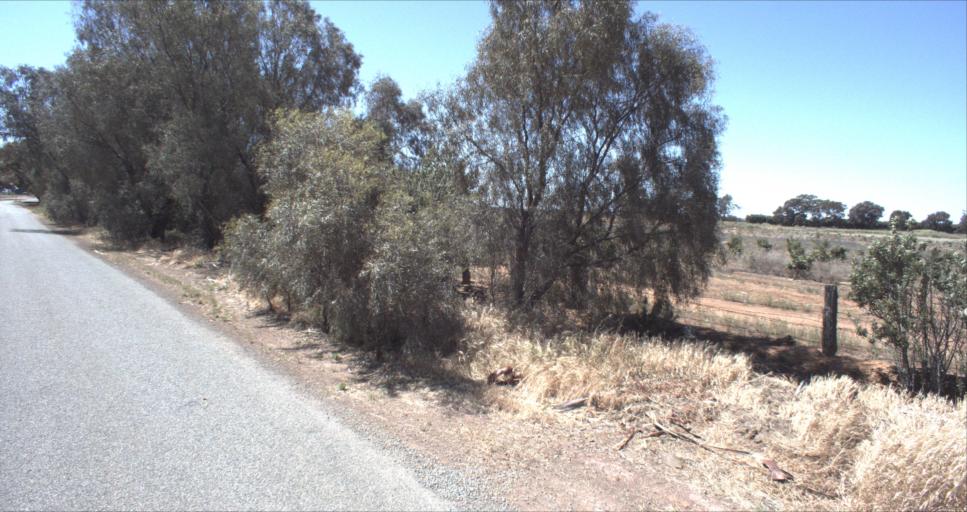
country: AU
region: New South Wales
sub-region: Leeton
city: Leeton
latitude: -34.5266
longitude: 146.3461
